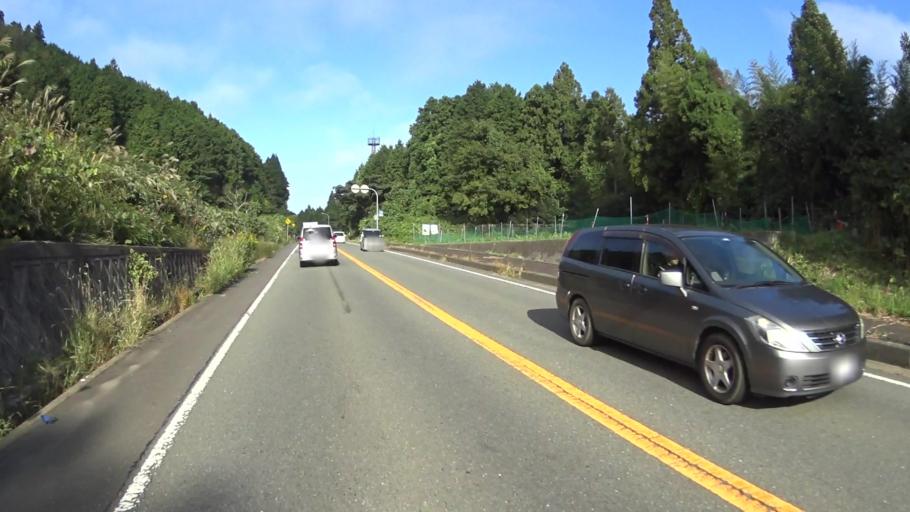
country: JP
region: Kyoto
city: Ayabe
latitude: 35.2671
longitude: 135.3769
